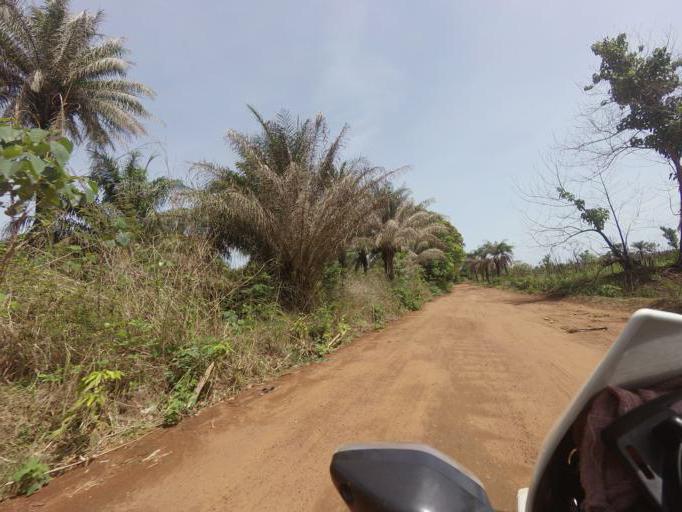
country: SL
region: Northern Province
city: Kamakwie
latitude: 9.4099
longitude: -12.2533
